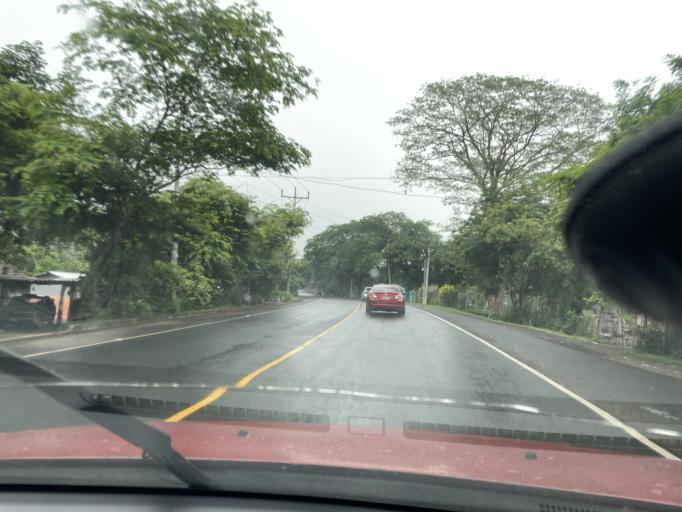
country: SV
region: San Miguel
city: San Miguel
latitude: 13.5594
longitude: -88.1080
